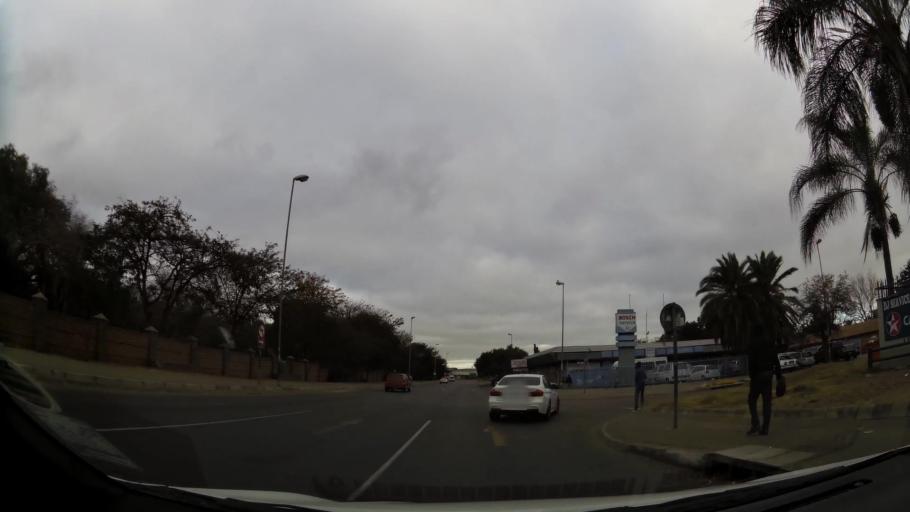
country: ZA
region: Limpopo
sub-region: Capricorn District Municipality
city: Polokwane
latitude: -23.9060
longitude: 29.4449
